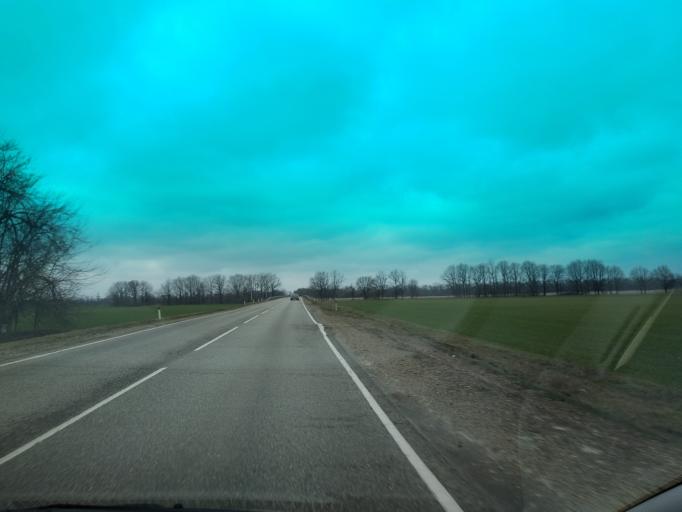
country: RU
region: Krasnodarskiy
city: Novorozhdestvenskaya
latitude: 45.7681
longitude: 39.9511
